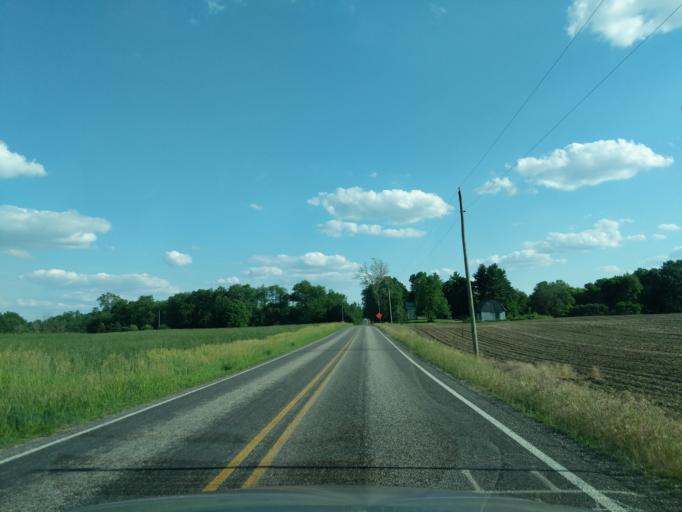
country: US
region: Indiana
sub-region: Kosciusko County
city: North Webster
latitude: 41.3007
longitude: -85.6431
